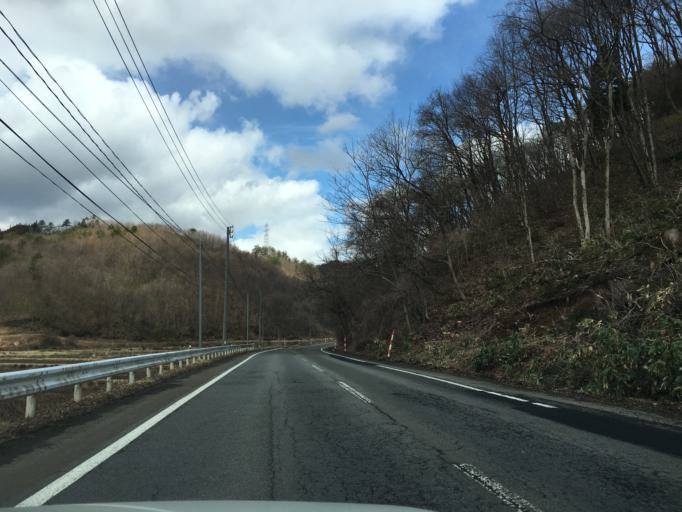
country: JP
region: Akita
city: Odate
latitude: 40.1831
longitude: 140.5002
